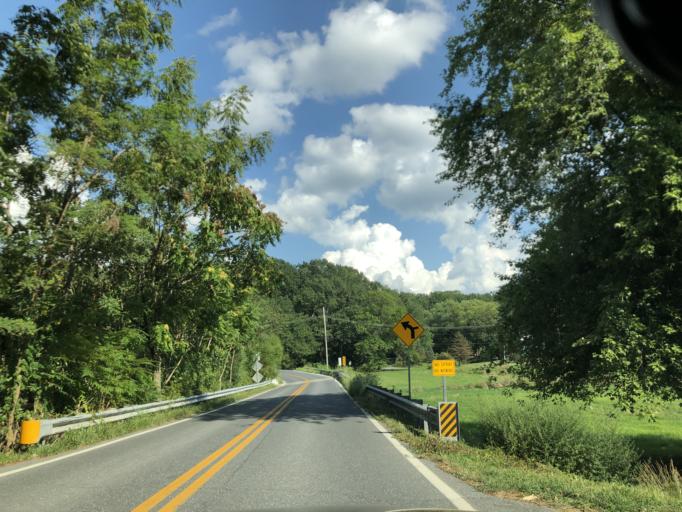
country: US
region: Maryland
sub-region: Frederick County
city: Linganore
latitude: 39.4693
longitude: -77.1701
